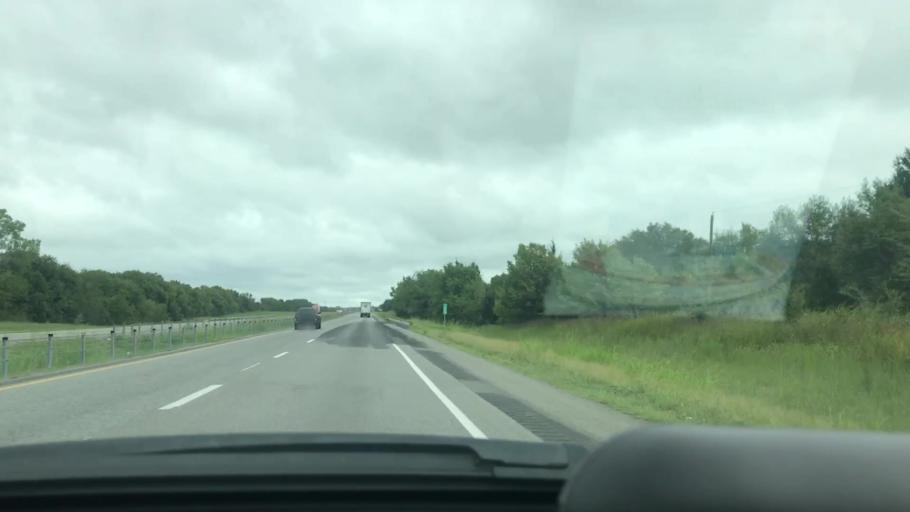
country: US
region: Oklahoma
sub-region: Pittsburg County
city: McAlester
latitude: 34.8041
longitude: -95.8650
